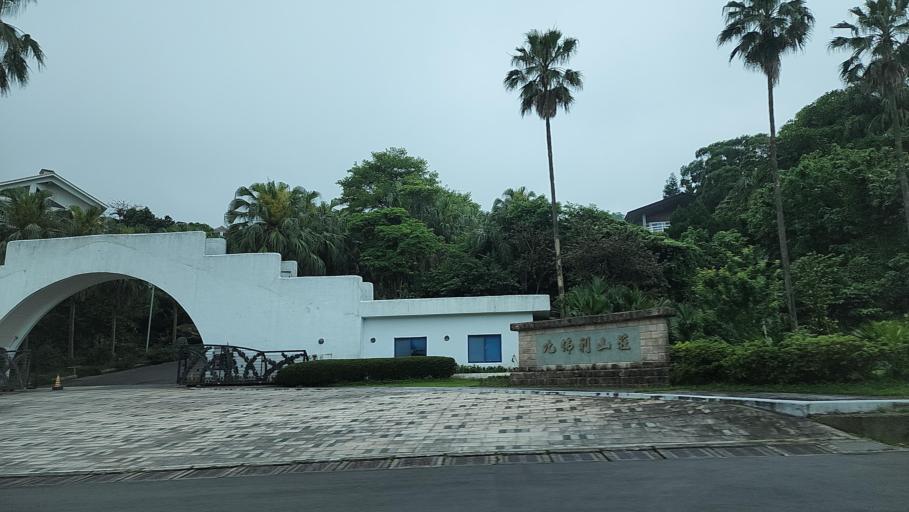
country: TW
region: Taiwan
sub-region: Keelung
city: Keelung
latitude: 25.1909
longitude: 121.6798
